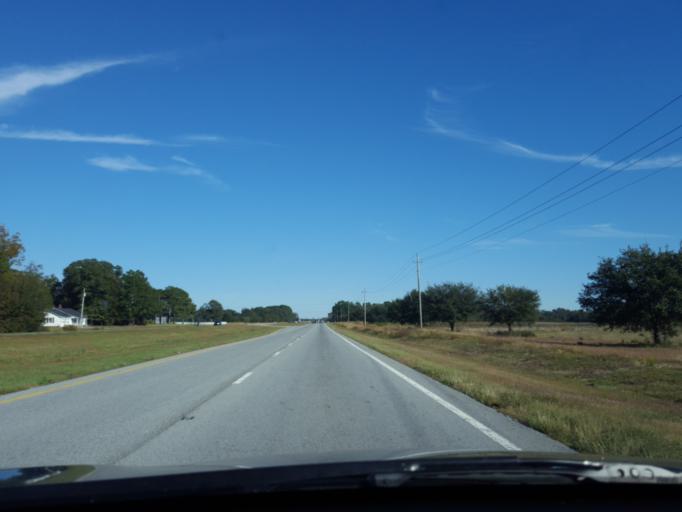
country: US
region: North Carolina
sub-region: Pitt County
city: Greenville
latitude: 35.6256
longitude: -77.2941
